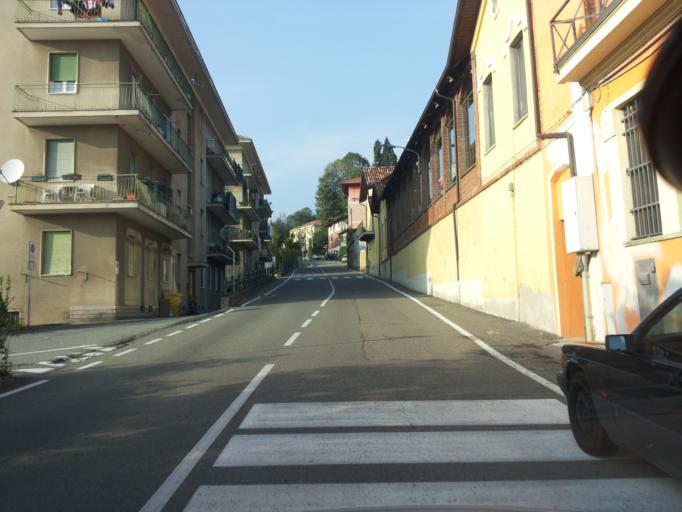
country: IT
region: Piedmont
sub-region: Provincia di Biella
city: Biella
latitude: 45.5601
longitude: 8.0441
